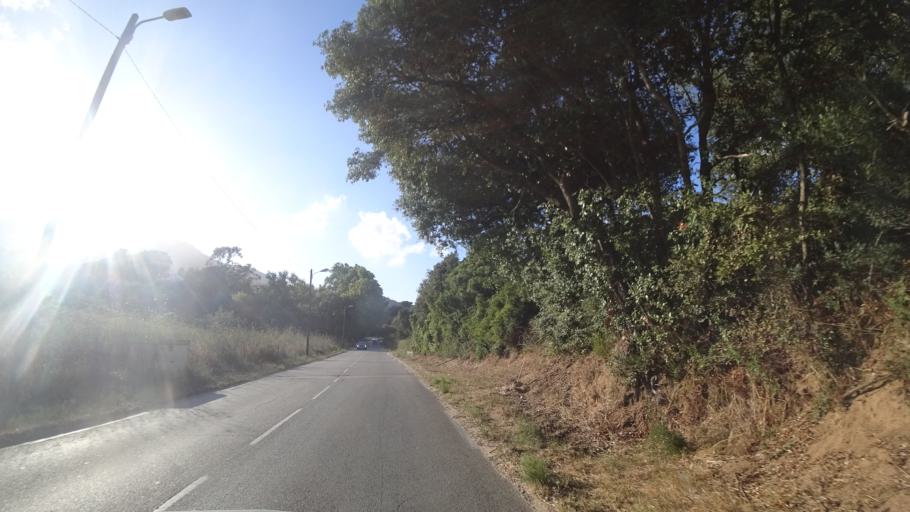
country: FR
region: Corsica
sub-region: Departement de la Corse-du-Sud
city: Ajaccio
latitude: 41.9508
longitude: 8.7337
